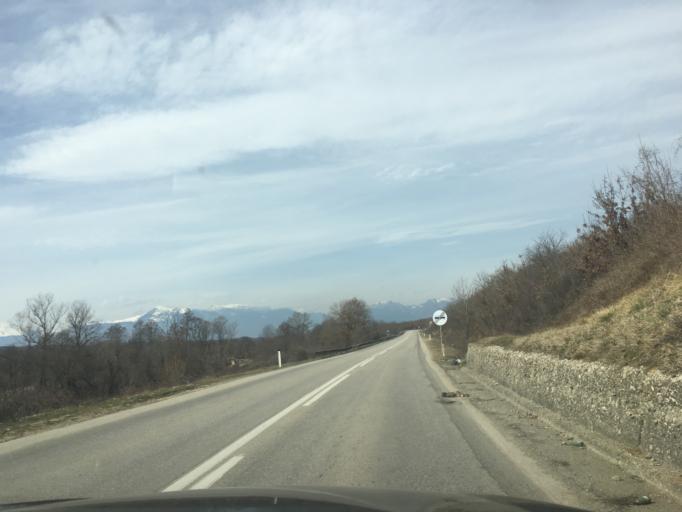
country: XK
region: Pec
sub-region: Komuna e Klines
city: Klina
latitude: 42.5937
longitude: 20.5442
